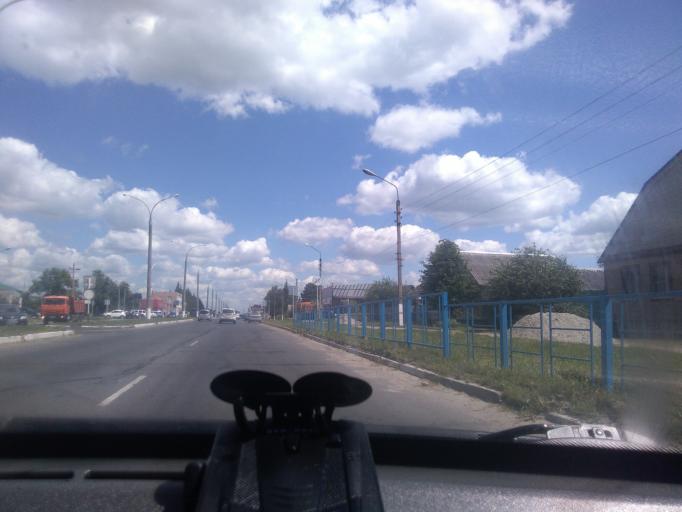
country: RU
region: Kursk
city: Pryamitsyno
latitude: 51.6568
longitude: 35.9347
